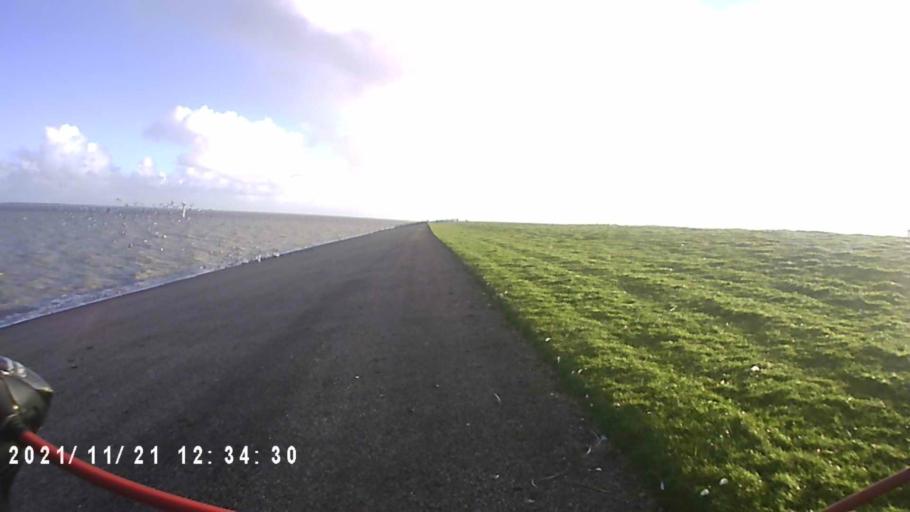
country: NL
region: Friesland
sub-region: Gemeente Dongeradeel
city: Anjum
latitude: 53.4059
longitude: 6.0584
